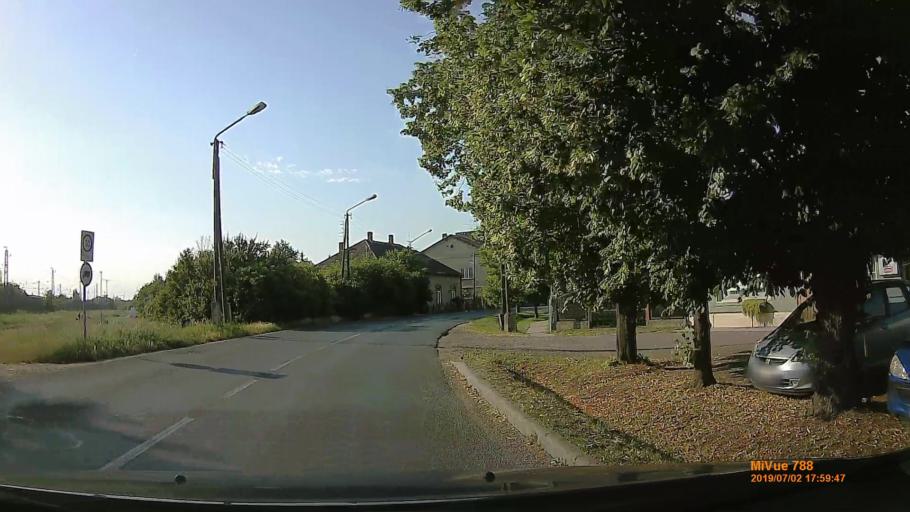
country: HU
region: Gyor-Moson-Sopron
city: Mosonmagyarovar
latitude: 47.8518
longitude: 17.2650
